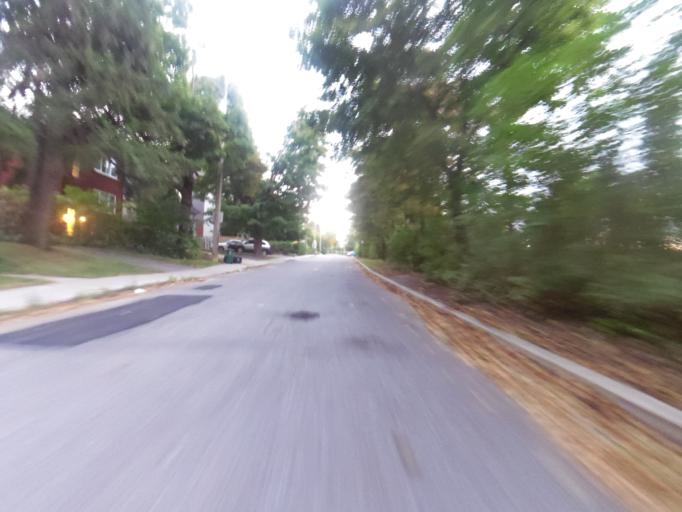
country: CA
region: Ontario
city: Ottawa
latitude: 45.4054
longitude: -75.6803
